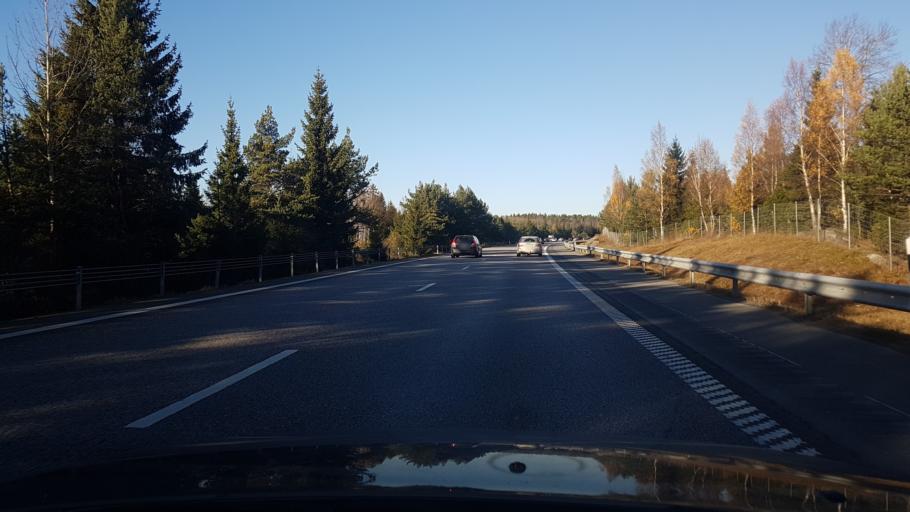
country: SE
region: Uppsala
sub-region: Knivsta Kommun
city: Knivsta
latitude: 59.7051
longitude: 17.8539
